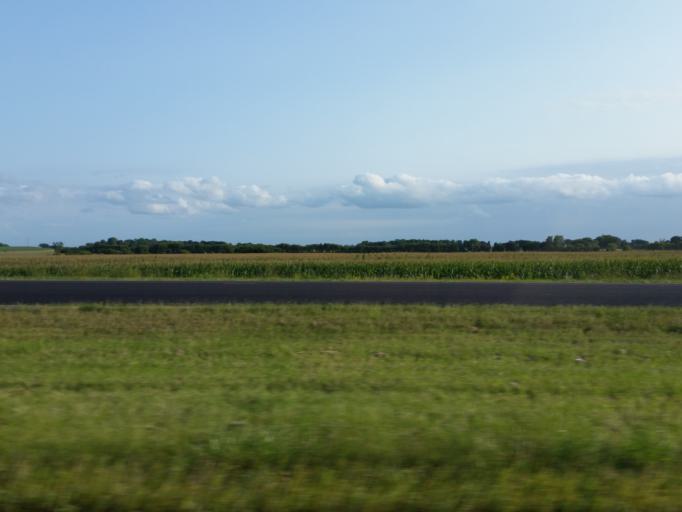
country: US
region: Wisconsin
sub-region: Pierce County
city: Prescott
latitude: 44.6009
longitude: -92.7678
